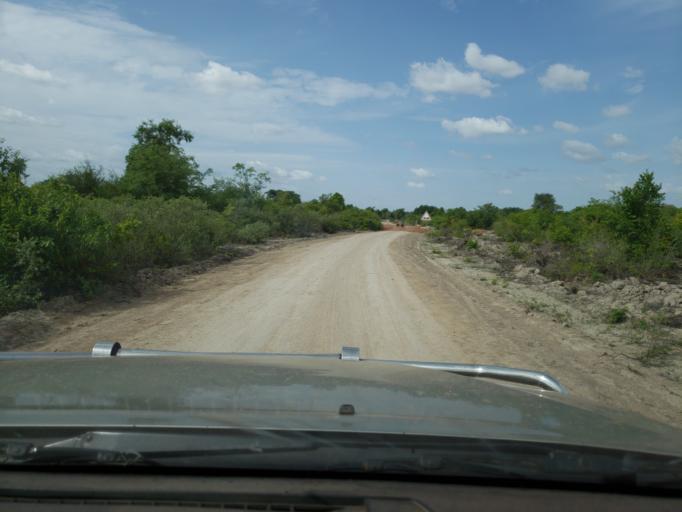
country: ML
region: Segou
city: Bla
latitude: 12.7674
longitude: -5.6200
